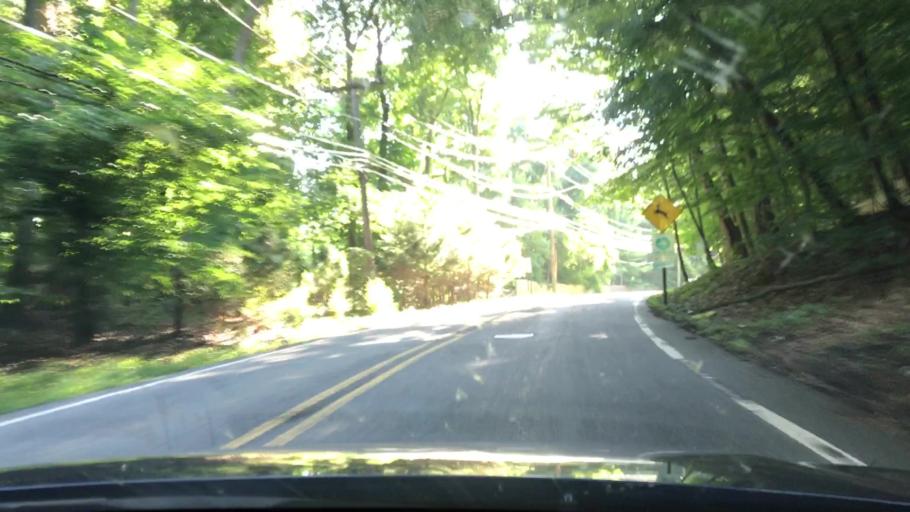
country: US
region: New Jersey
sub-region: Bergen County
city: Alpine
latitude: 40.9429
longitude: -73.9418
